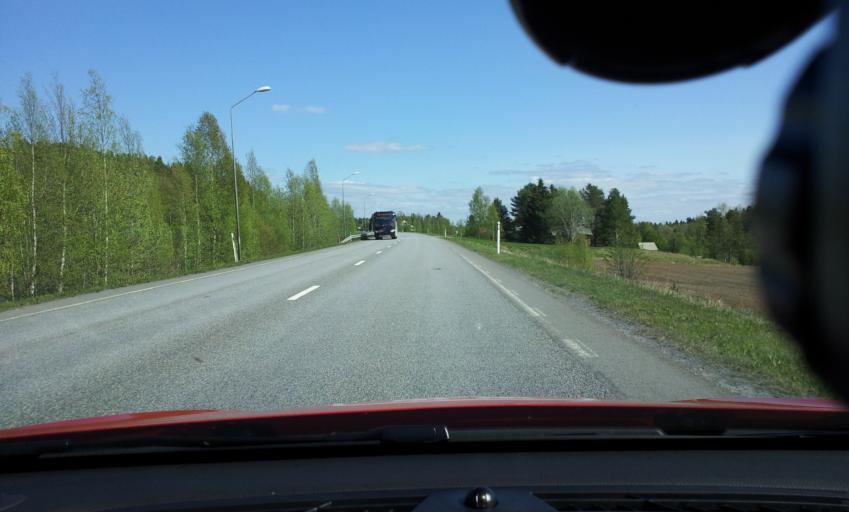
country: SE
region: Jaemtland
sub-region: Krokoms Kommun
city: Valla
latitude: 63.3209
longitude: 14.0657
